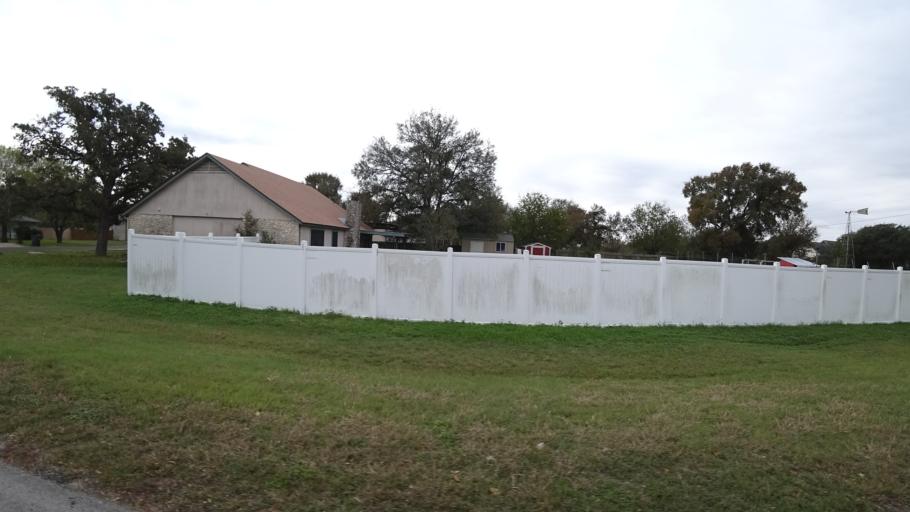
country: US
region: Texas
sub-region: Travis County
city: Shady Hollow
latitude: 30.1482
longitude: -97.8778
